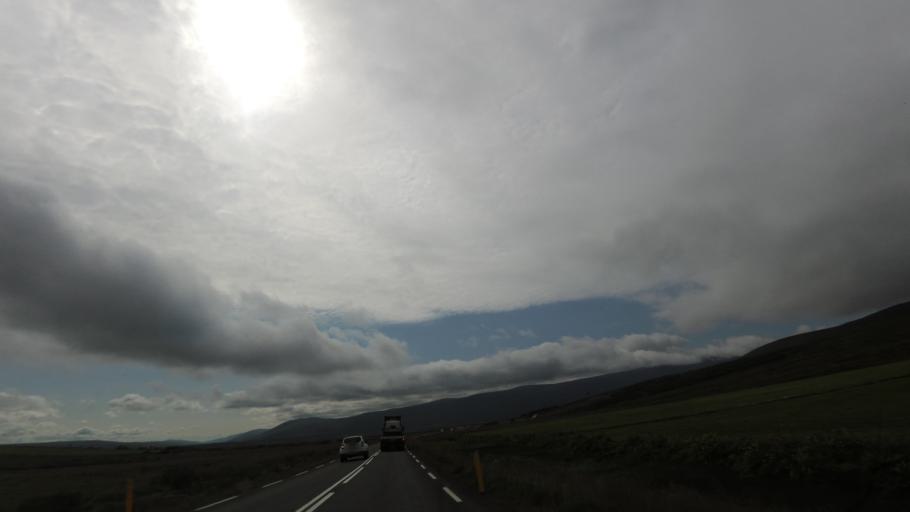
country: IS
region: Northeast
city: Laugar
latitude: 65.7329
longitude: -17.5909
